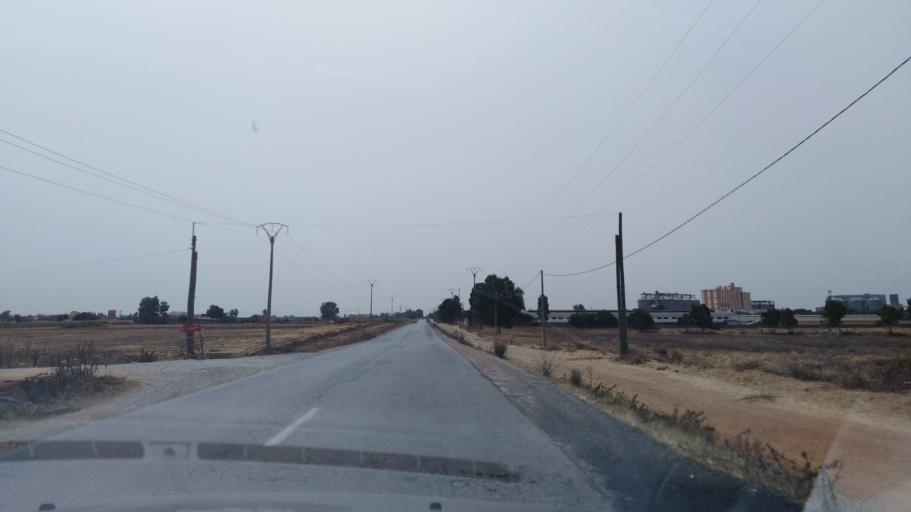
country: MA
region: Grand Casablanca
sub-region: Nouaceur
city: Dar Bouazza
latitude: 33.3765
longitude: -7.7852
